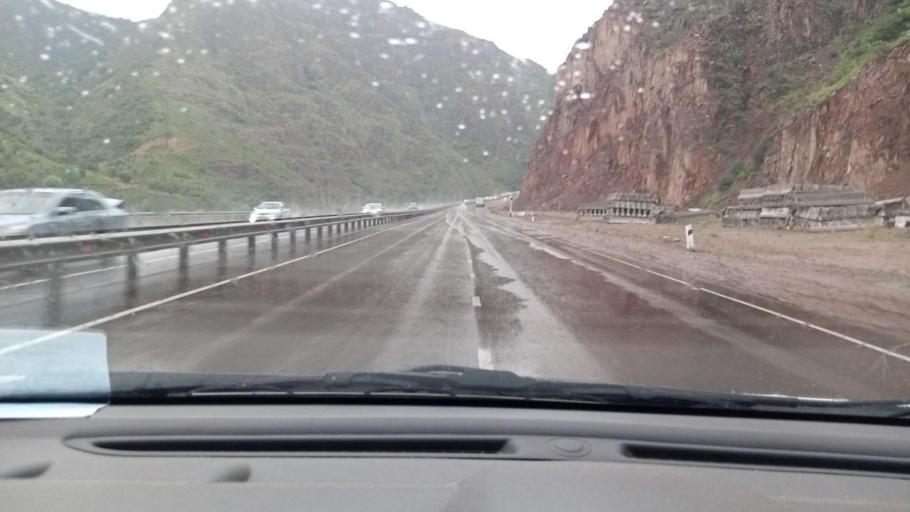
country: UZ
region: Toshkent
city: Angren
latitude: 41.0888
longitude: 70.3212
